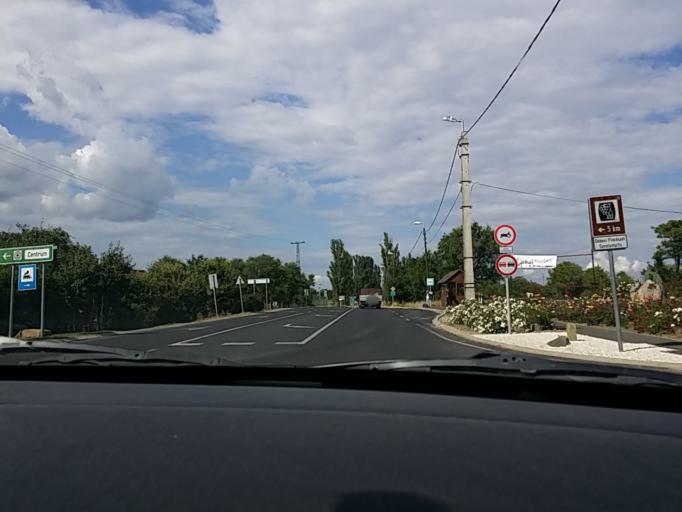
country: HU
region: Veszprem
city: Zanka
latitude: 46.8726
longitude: 17.6834
